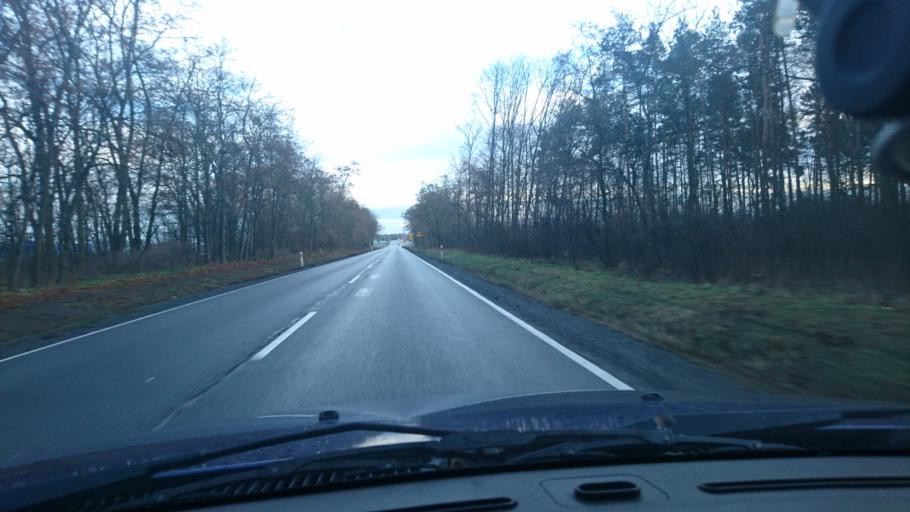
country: PL
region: Greater Poland Voivodeship
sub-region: Powiat kepinski
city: Kepno
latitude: 51.3220
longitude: 17.9713
